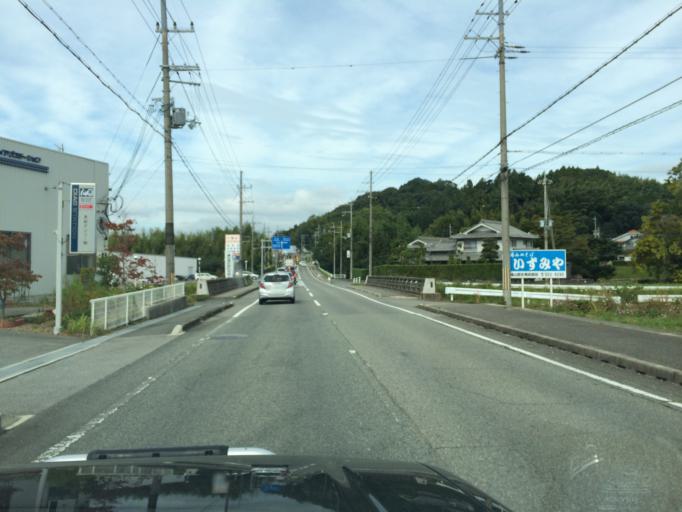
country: JP
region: Hyogo
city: Sasayama
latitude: 35.0733
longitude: 135.2075
